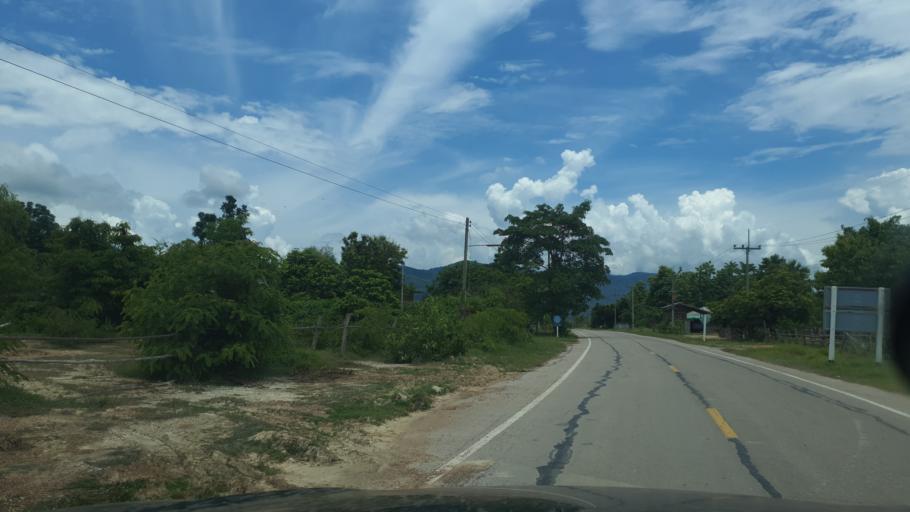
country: TH
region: Lampang
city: Sop Prap
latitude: 17.9209
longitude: 99.4112
